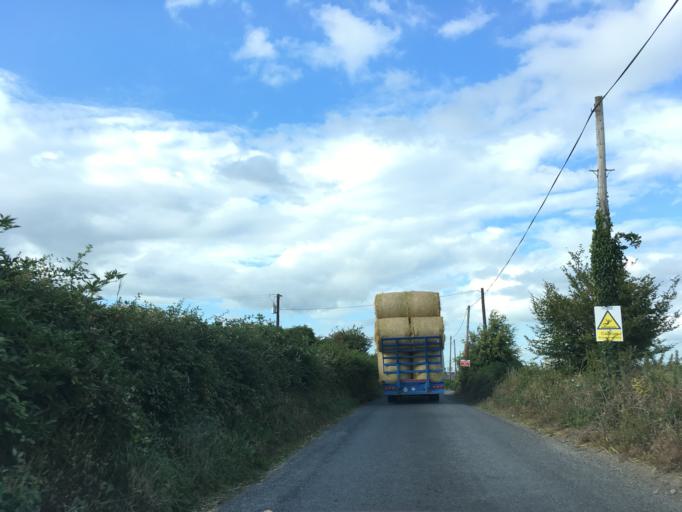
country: IE
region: Munster
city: Cahir
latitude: 52.2987
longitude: -7.9476
